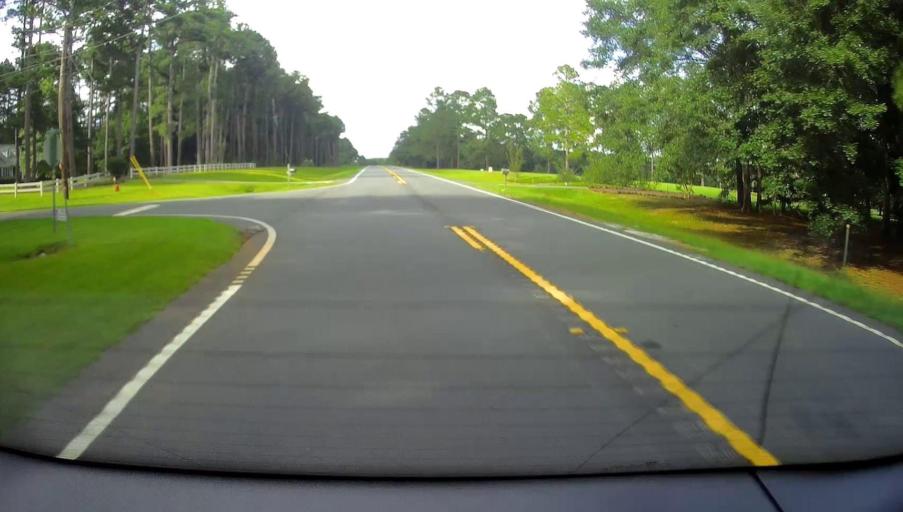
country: US
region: Georgia
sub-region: Meriwether County
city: Manchester
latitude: 32.9709
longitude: -84.6004
